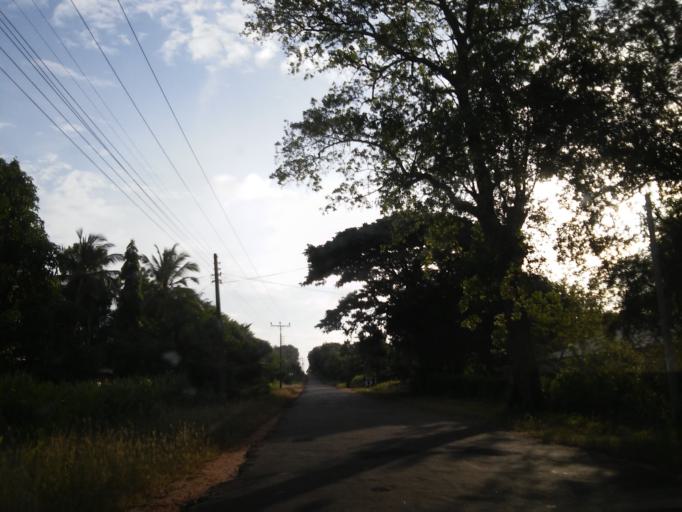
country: LK
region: Central
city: Sigiriya
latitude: 8.1377
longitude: 80.6365
